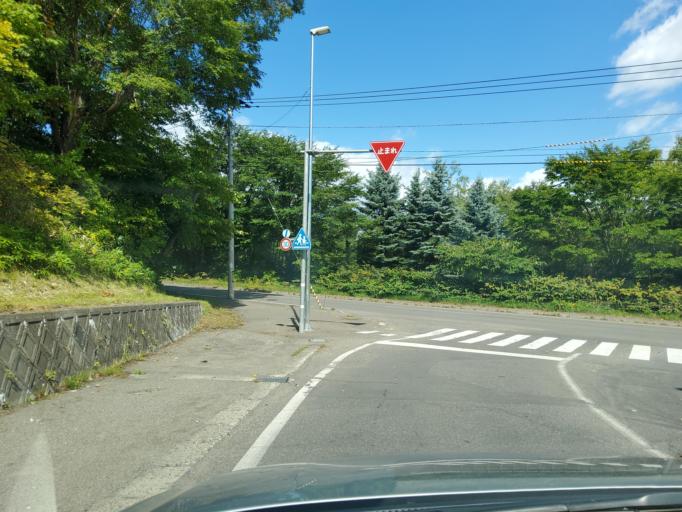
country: JP
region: Hokkaido
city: Obihiro
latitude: 42.9524
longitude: 143.1975
